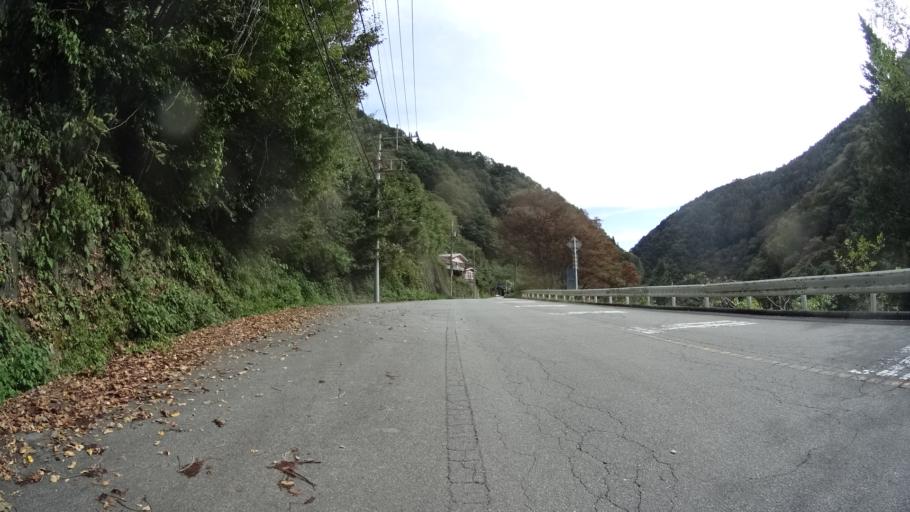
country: JP
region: Yamanashi
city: Otsuki
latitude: 35.7859
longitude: 138.9666
